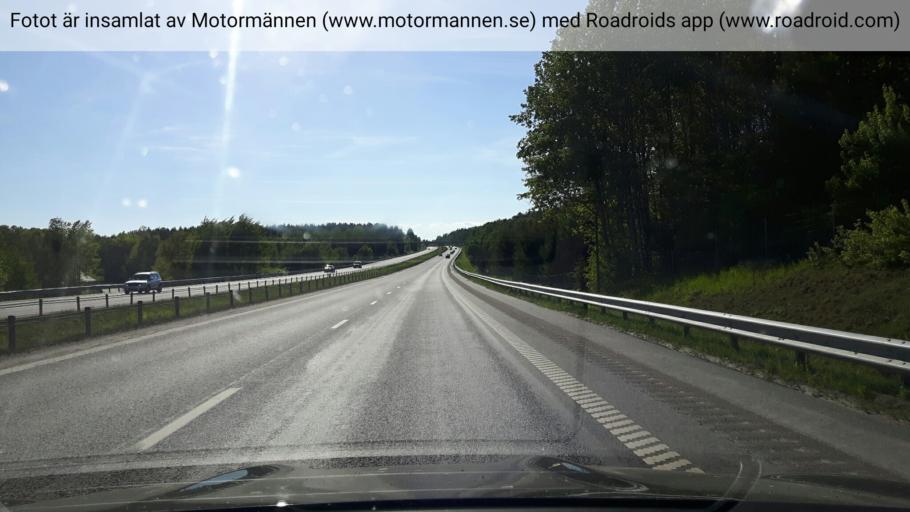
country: SE
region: Stockholm
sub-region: Norrtalje Kommun
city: Norrtalje
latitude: 59.7422
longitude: 18.6567
